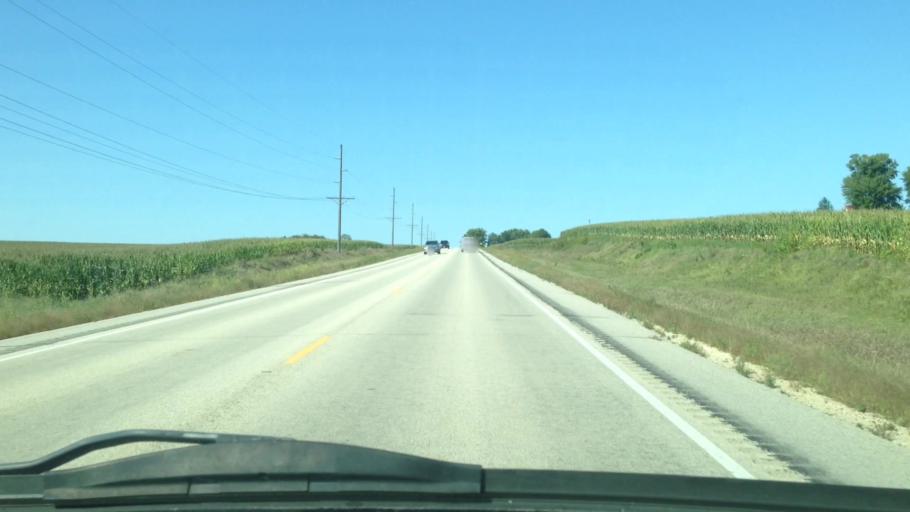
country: US
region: Minnesota
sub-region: Fillmore County
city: Rushford
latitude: 43.9130
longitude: -91.7401
